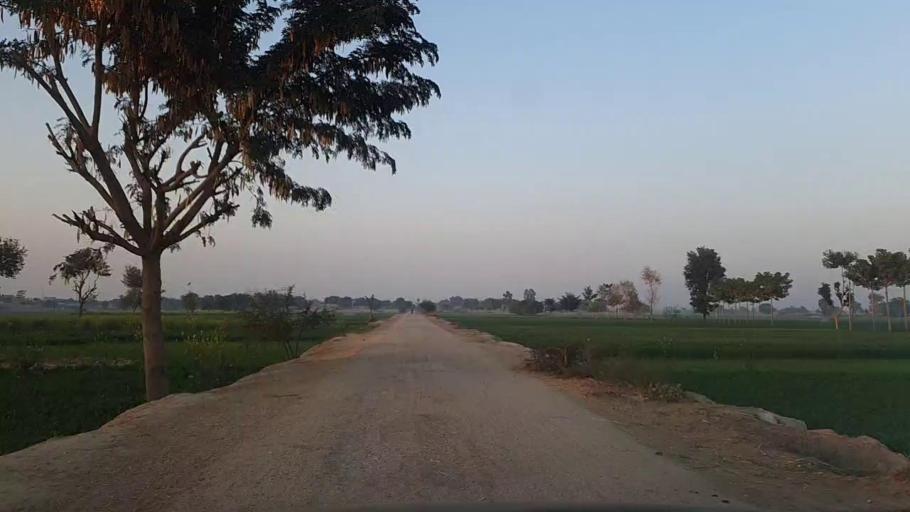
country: PK
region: Sindh
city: Jam Sahib
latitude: 26.4660
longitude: 68.5420
